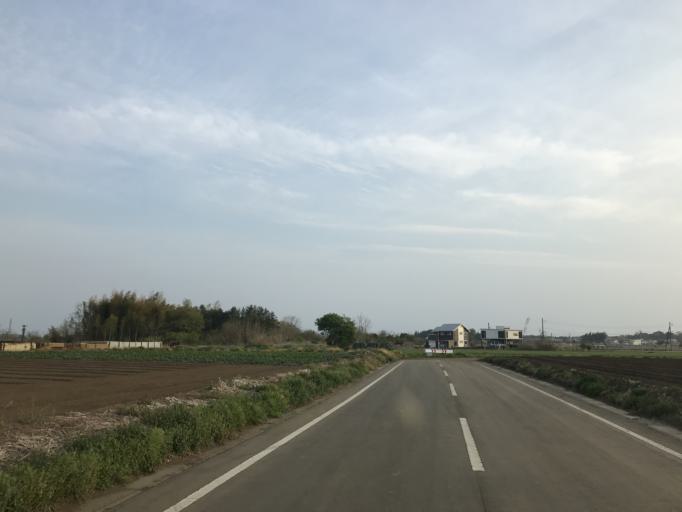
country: JP
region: Ibaraki
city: Tsukuba
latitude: 36.1210
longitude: 140.0827
